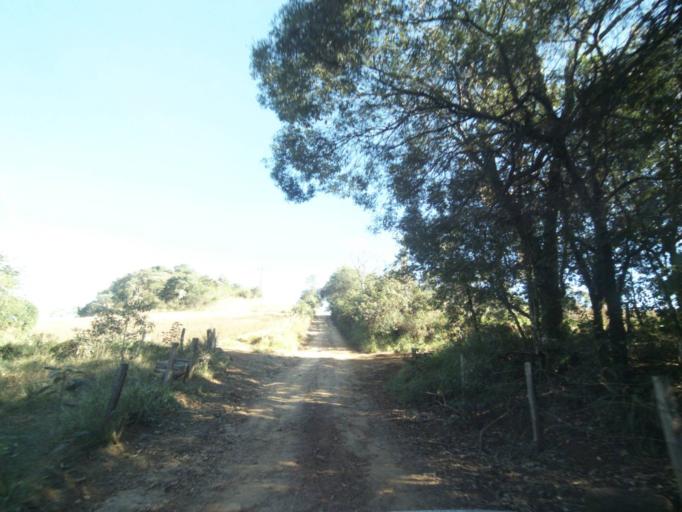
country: BR
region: Parana
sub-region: Tibagi
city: Tibagi
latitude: -24.5713
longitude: -50.4726
